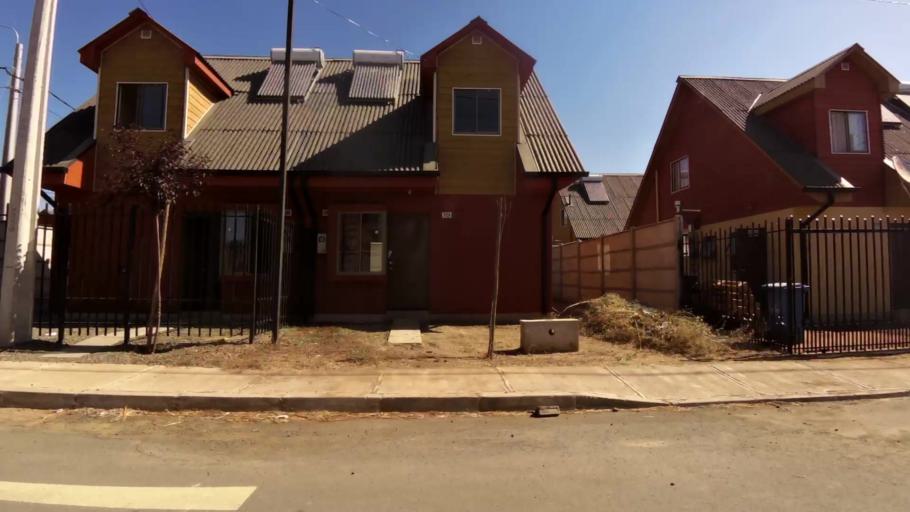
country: CL
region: Maule
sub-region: Provincia de Talca
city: Talca
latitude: -35.4065
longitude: -71.6202
